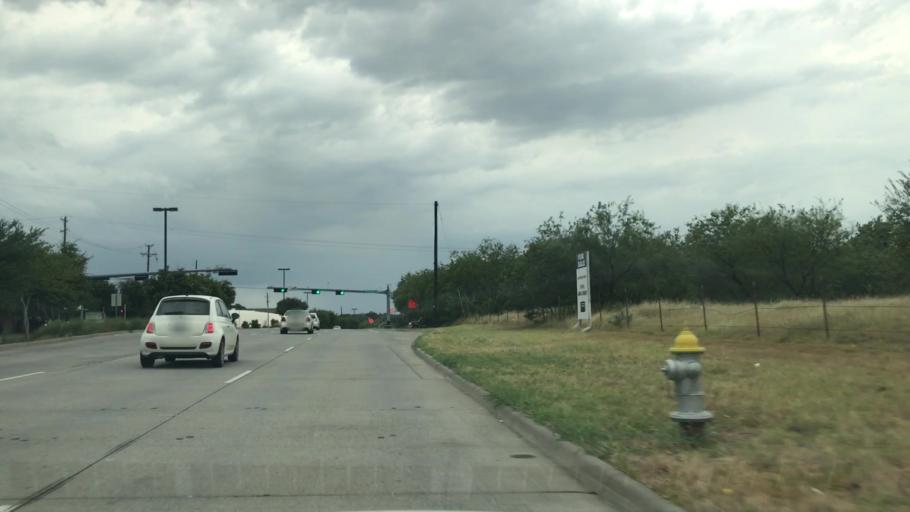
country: US
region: Texas
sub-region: Dallas County
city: Carrollton
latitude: 32.9767
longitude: -96.9101
